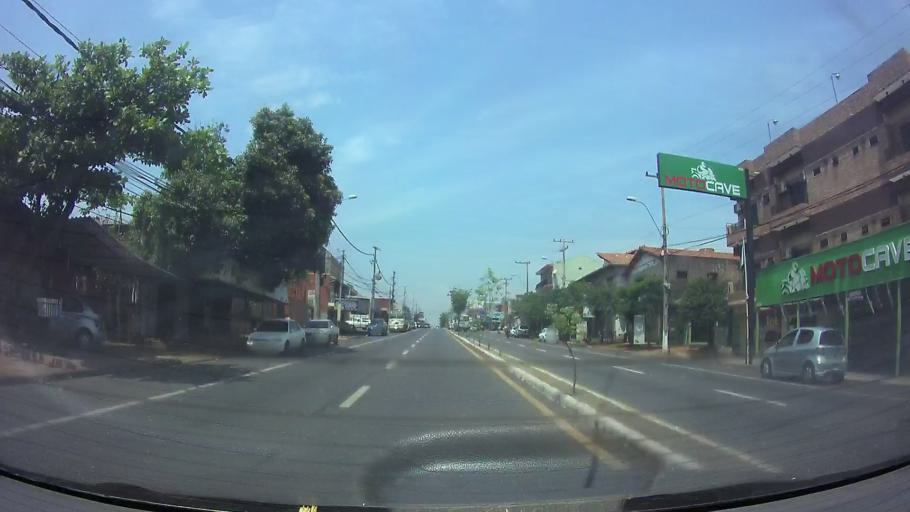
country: PY
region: Central
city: Itaugua
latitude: -25.3903
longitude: -57.3585
